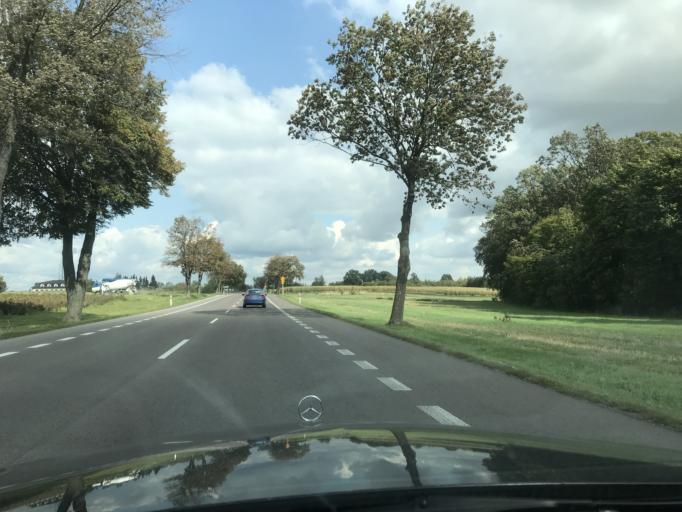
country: PL
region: Lublin Voivodeship
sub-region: Powiat lubelski
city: Kozubszczyzna
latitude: 51.1740
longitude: 22.4207
